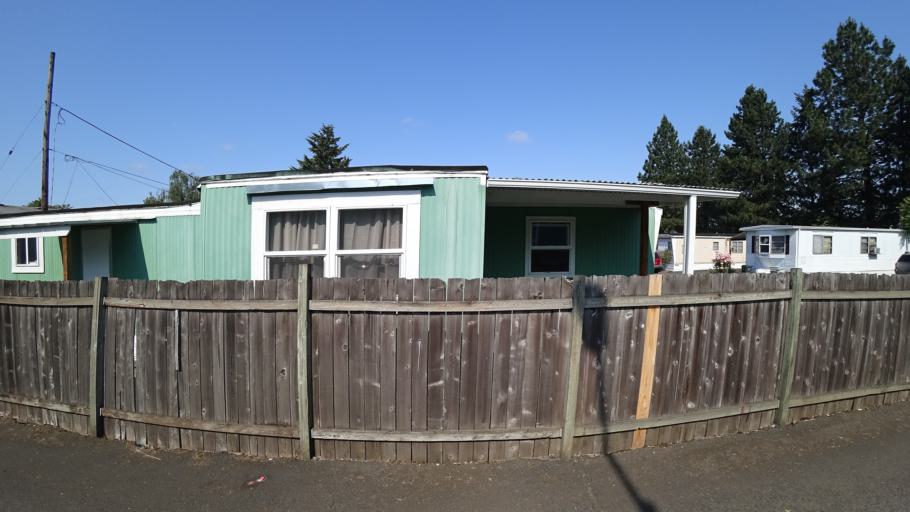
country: US
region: Oregon
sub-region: Multnomah County
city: Lents
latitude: 45.4580
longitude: -122.5835
